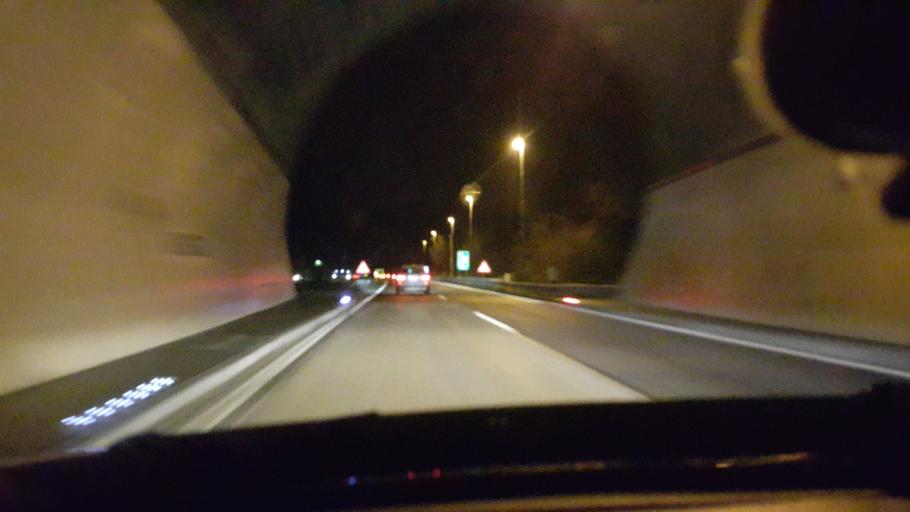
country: SI
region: Slovenska Konjice
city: Slovenske Konjice
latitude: 46.2981
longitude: 15.4425
